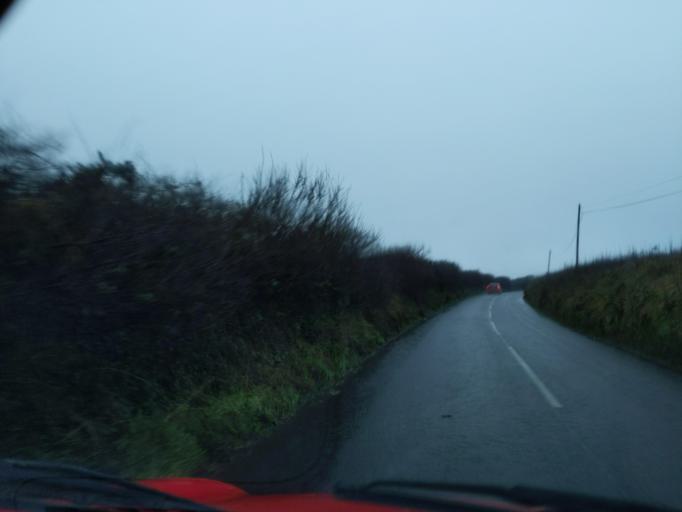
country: GB
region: England
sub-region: Cornwall
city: Camelford
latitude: 50.6393
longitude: -4.6929
